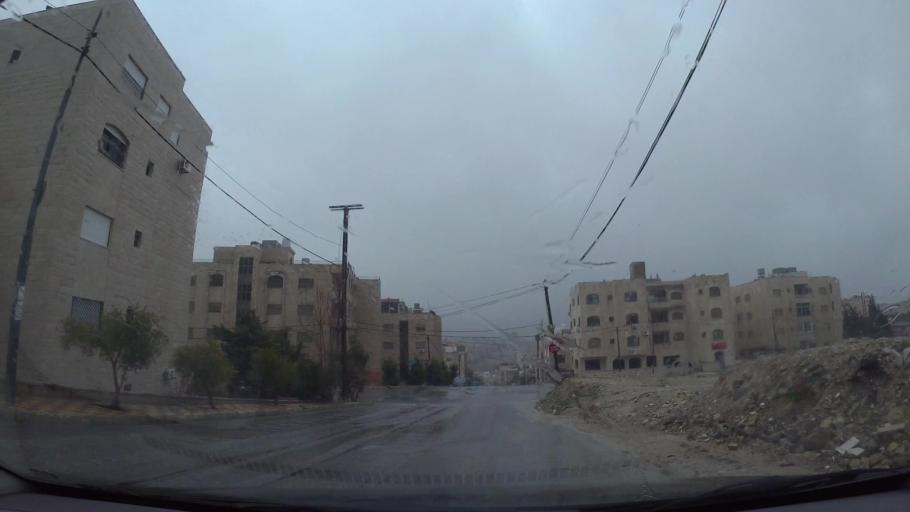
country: JO
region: Amman
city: Al Jubayhah
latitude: 32.0156
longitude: 35.8859
